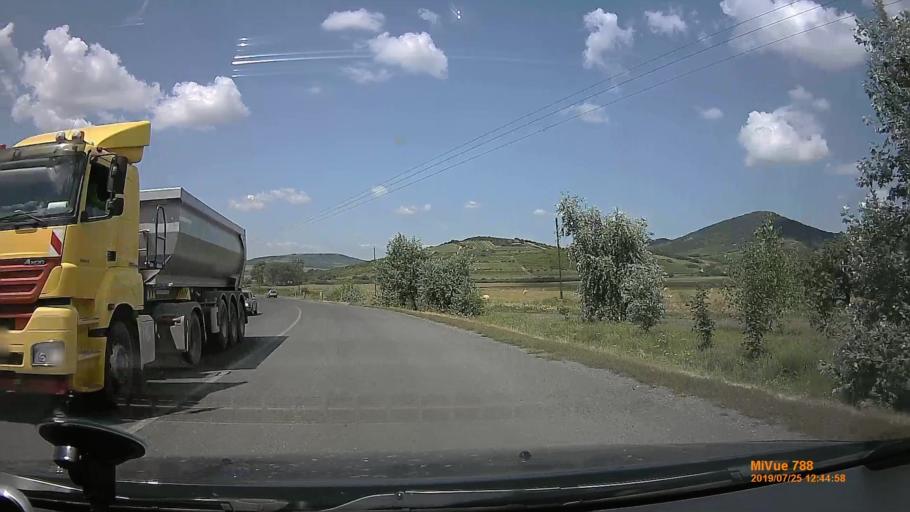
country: HU
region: Borsod-Abauj-Zemplen
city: Tallya
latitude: 48.2397
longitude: 21.2112
